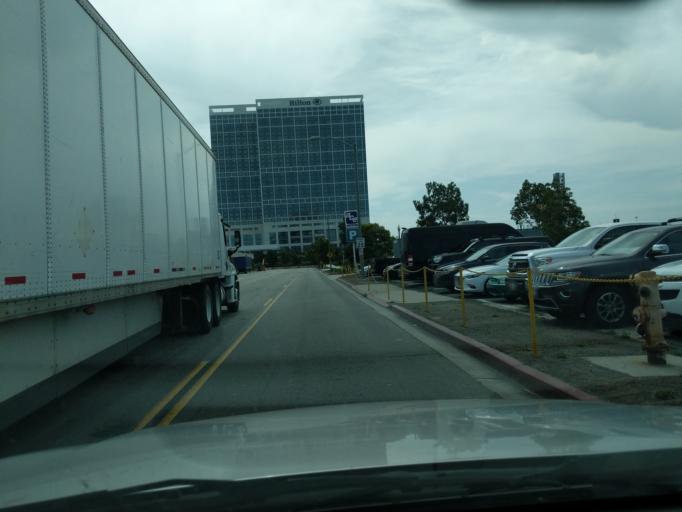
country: US
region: California
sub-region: San Diego County
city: San Diego
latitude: 32.7055
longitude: -117.1619
